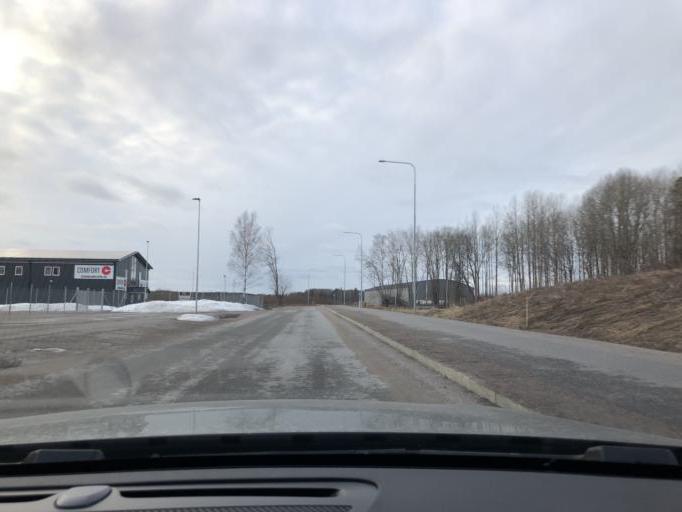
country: SE
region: Uppsala
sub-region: Tierps Kommun
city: Tierp
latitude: 60.3488
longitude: 17.4971
